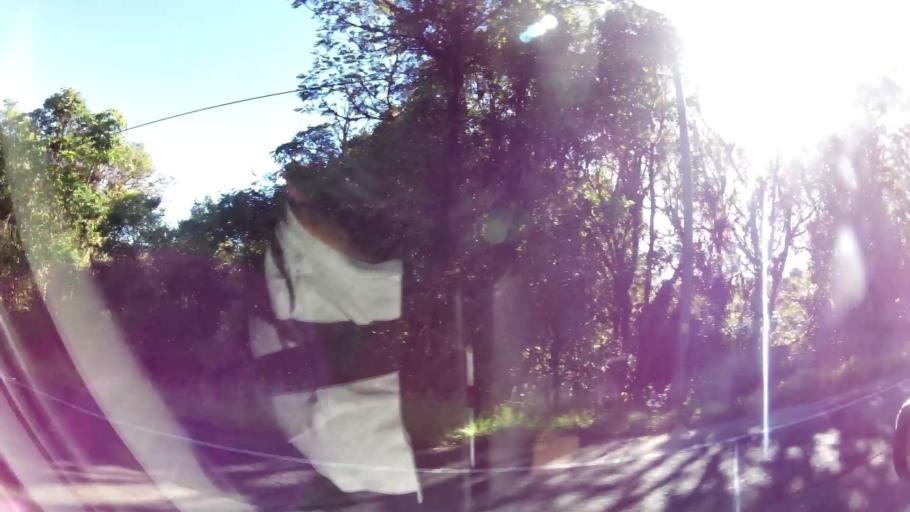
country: CR
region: San Jose
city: San Marcos
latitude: 9.7101
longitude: -83.9477
